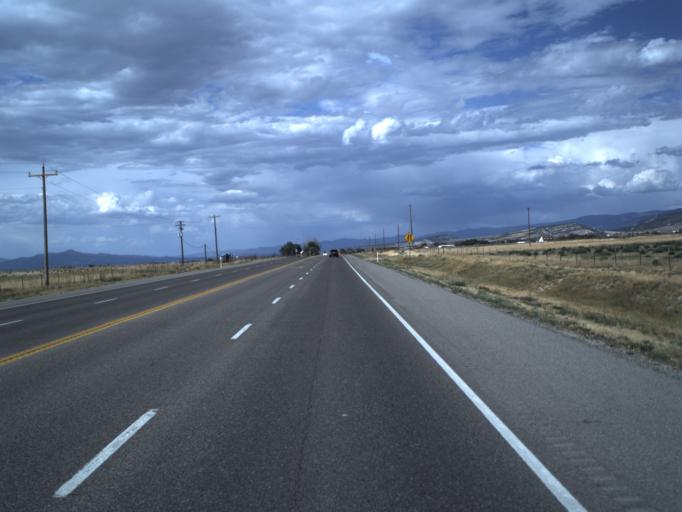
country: US
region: Utah
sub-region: Sanpete County
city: Ephraim
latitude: 39.3196
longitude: -111.6067
